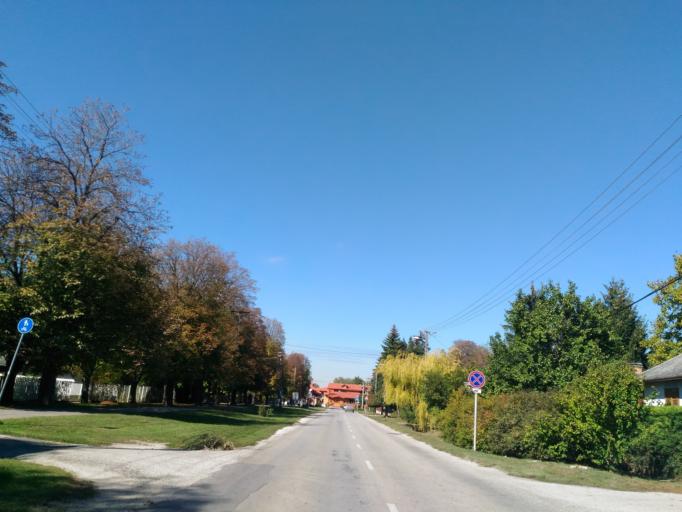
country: HU
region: Fejer
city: Gardony
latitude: 47.1959
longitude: 18.6108
